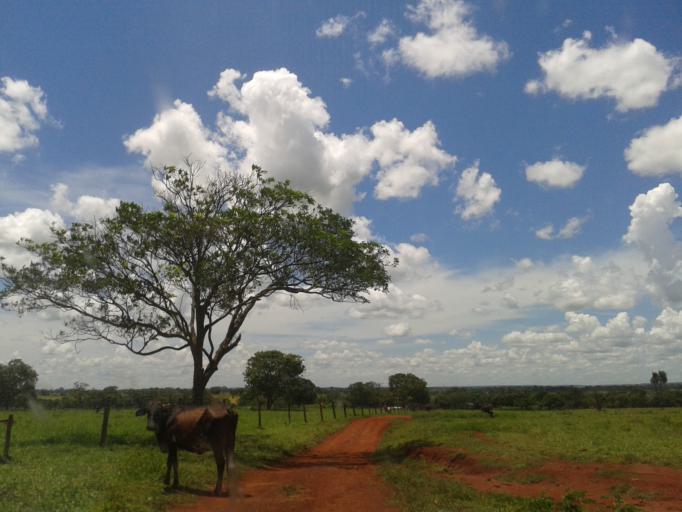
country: BR
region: Minas Gerais
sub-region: Capinopolis
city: Capinopolis
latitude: -18.7766
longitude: -49.8048
